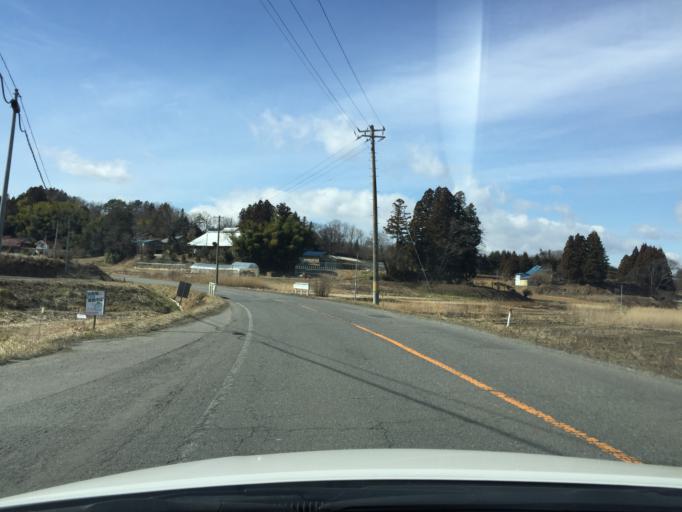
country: JP
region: Fukushima
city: Funehikimachi-funehiki
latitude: 37.4034
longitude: 140.5617
